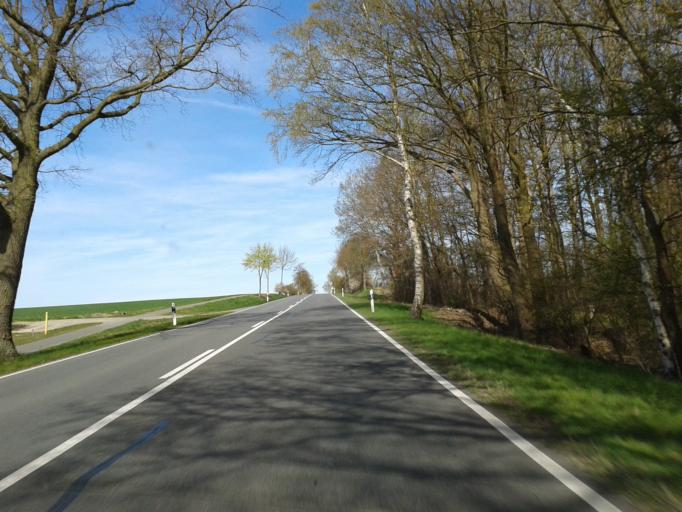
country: DE
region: Lower Saxony
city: Suhlendorf
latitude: 52.9429
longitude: 10.7373
